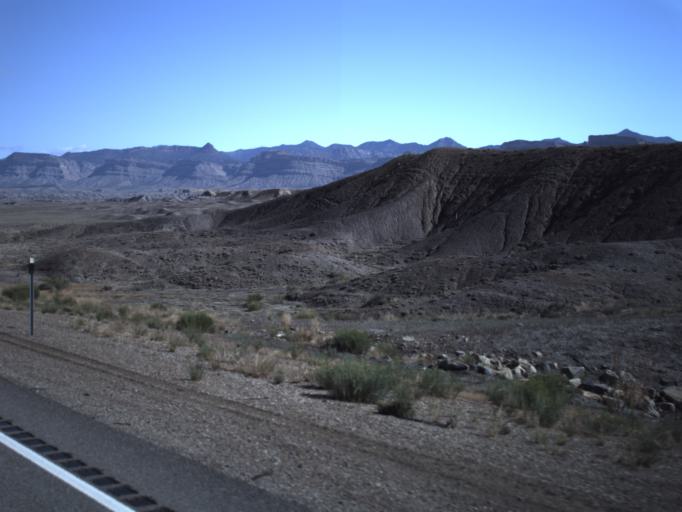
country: US
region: Utah
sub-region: Carbon County
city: East Carbon City
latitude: 39.3051
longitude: -110.3587
